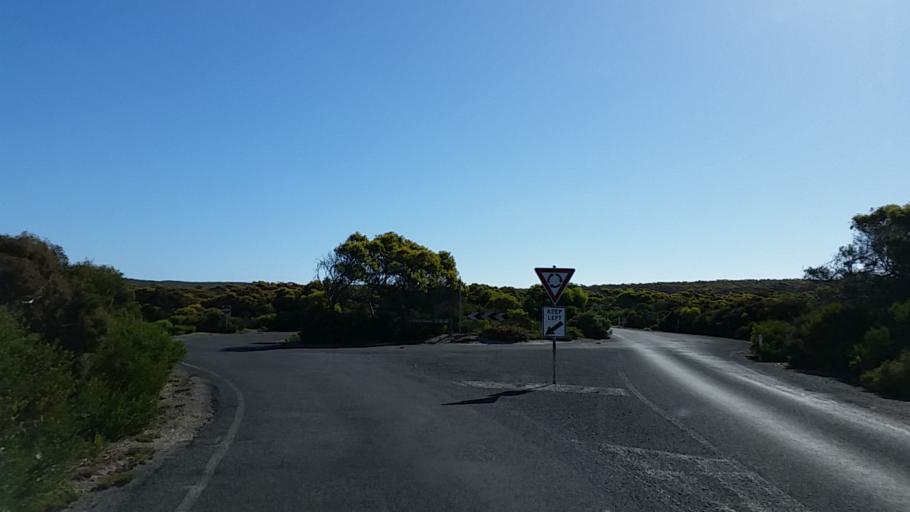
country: AU
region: South Australia
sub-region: Yorke Peninsula
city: Honiton
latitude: -35.2676
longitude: 136.9419
